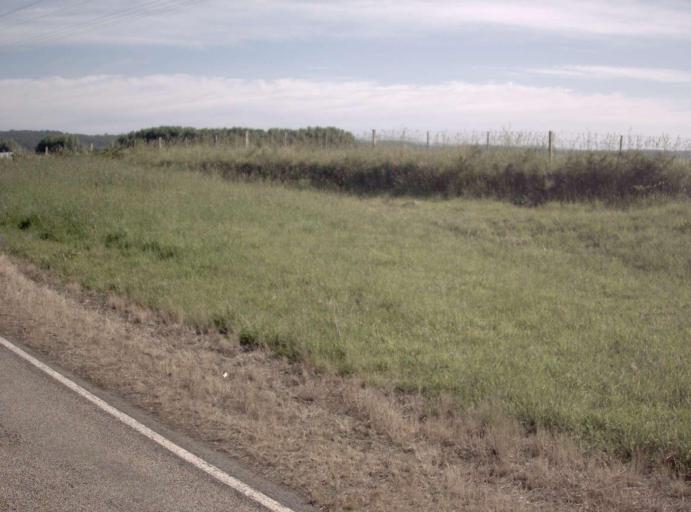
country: AU
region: Victoria
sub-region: East Gippsland
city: Bairnsdale
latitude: -37.7317
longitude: 147.8107
